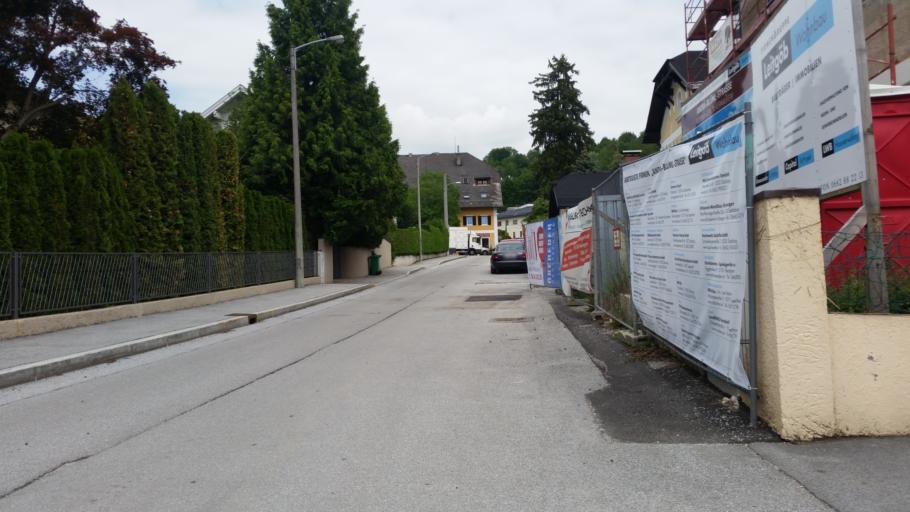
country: AT
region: Salzburg
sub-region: Salzburg Stadt
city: Salzburg
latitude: 47.8110
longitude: 13.0718
